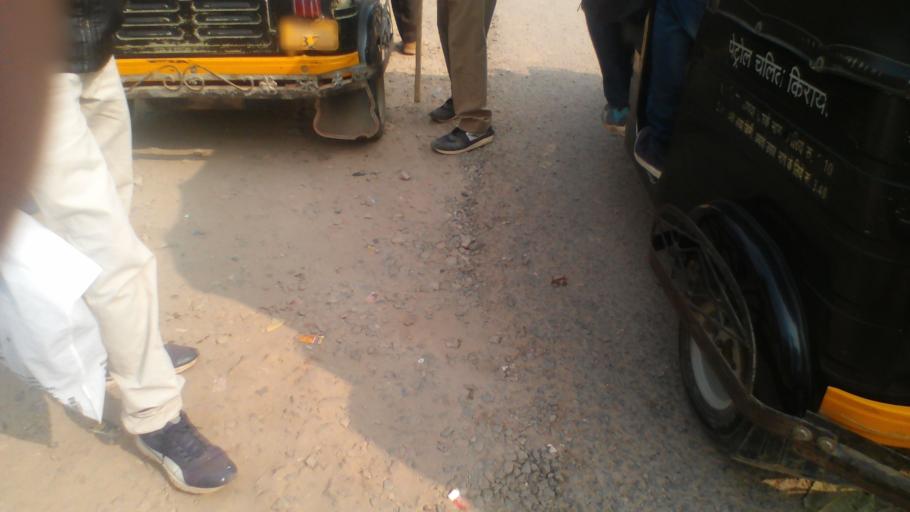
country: IN
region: Uttar Pradesh
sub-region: Varanasi
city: Varanasi
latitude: 25.3292
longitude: 82.9898
